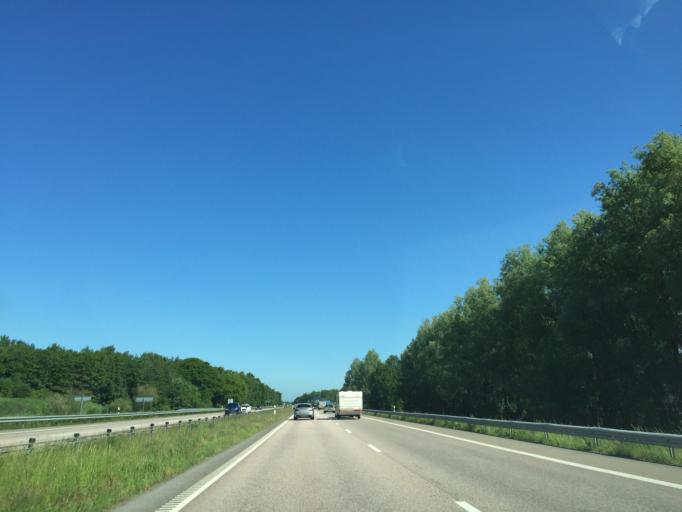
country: SE
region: Skane
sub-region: Helsingborg
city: Barslov
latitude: 56.0494
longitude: 12.7850
